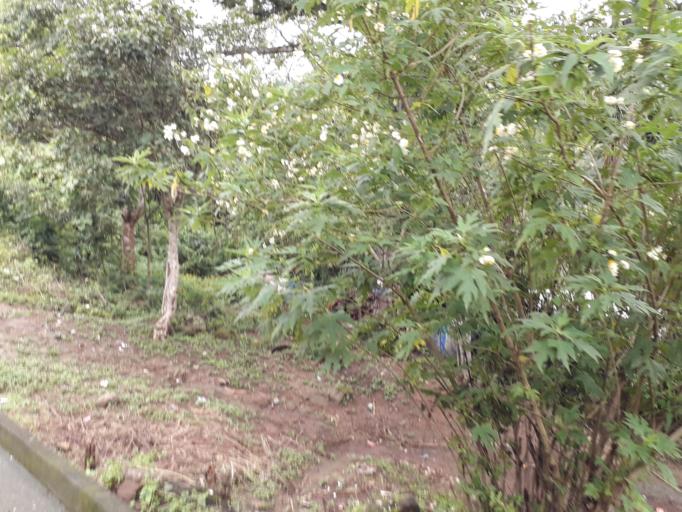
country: GT
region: Escuintla
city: Guanagazapa
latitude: 14.3127
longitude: -90.5593
